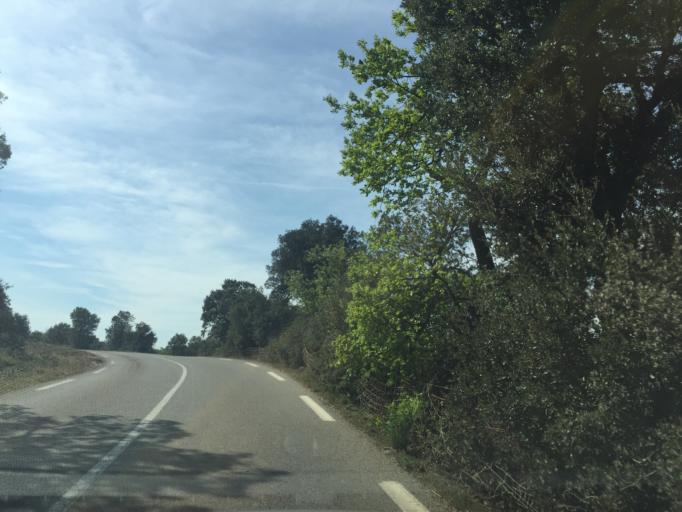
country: FR
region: Provence-Alpes-Cote d'Azur
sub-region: Departement du Var
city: Saint-Julien
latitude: 43.6647
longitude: 5.8957
